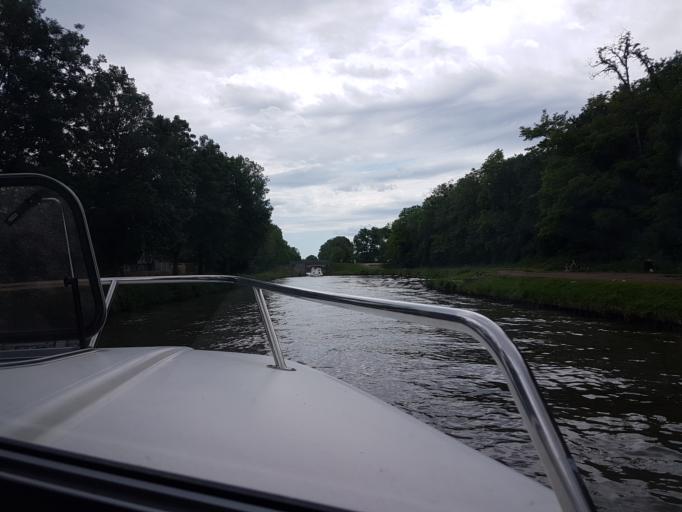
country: FR
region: Bourgogne
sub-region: Departement de la Nievre
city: Clamecy
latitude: 47.4842
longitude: 3.5242
